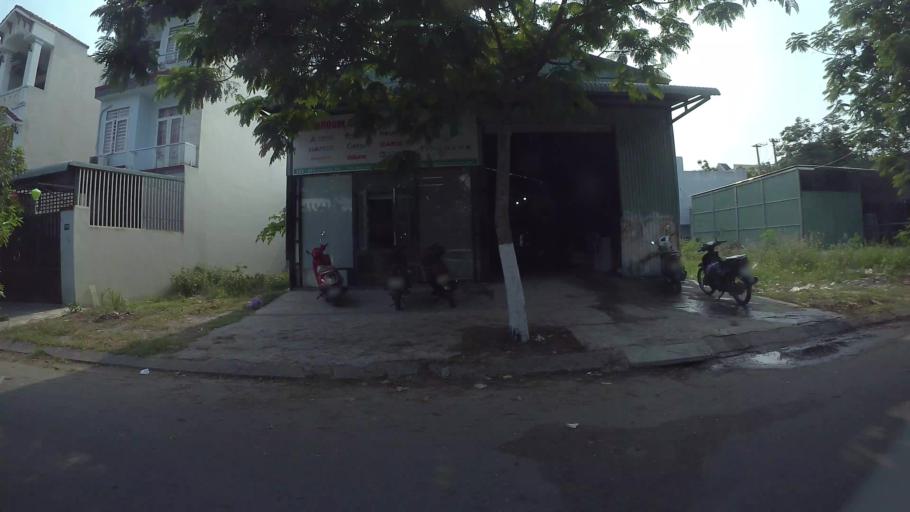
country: VN
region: Da Nang
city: Thanh Khe
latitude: 16.0472
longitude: 108.1744
